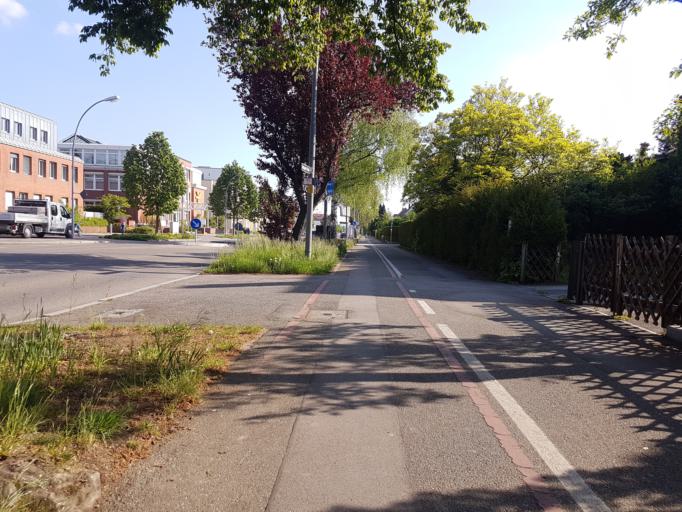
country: DE
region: Baden-Wuerttemberg
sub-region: Regierungsbezirk Stuttgart
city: Kornwestheim
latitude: 48.8579
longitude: 9.1851
